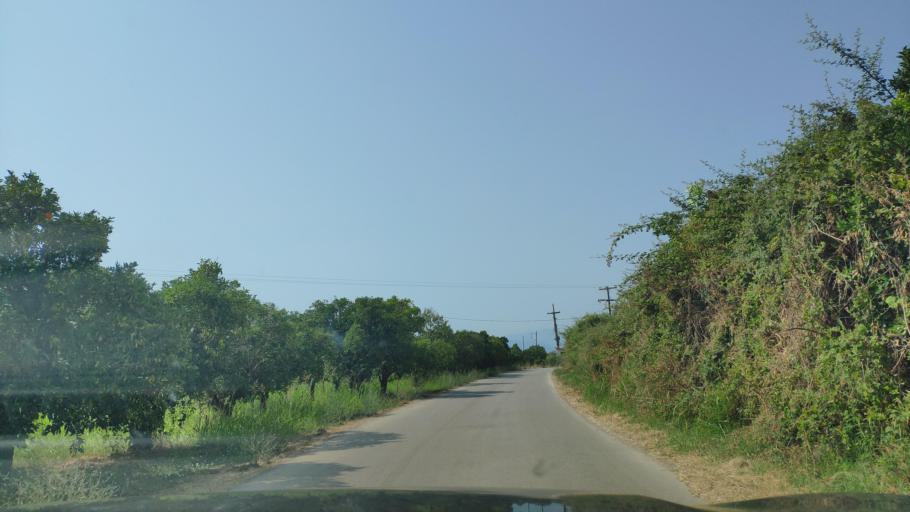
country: GR
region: Epirus
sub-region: Nomos Artas
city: Kompoti
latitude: 39.0742
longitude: 21.0827
